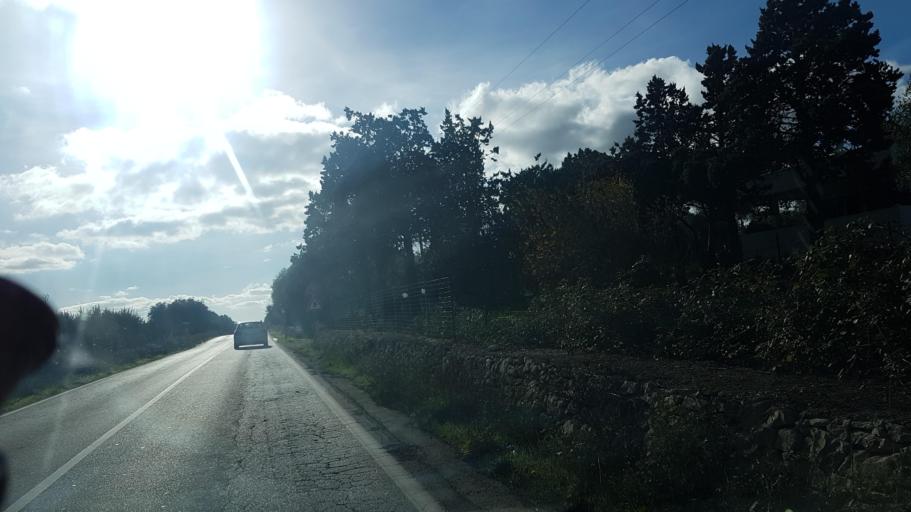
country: IT
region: Apulia
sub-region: Provincia di Brindisi
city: Ostuni
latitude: 40.6882
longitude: 17.5517
